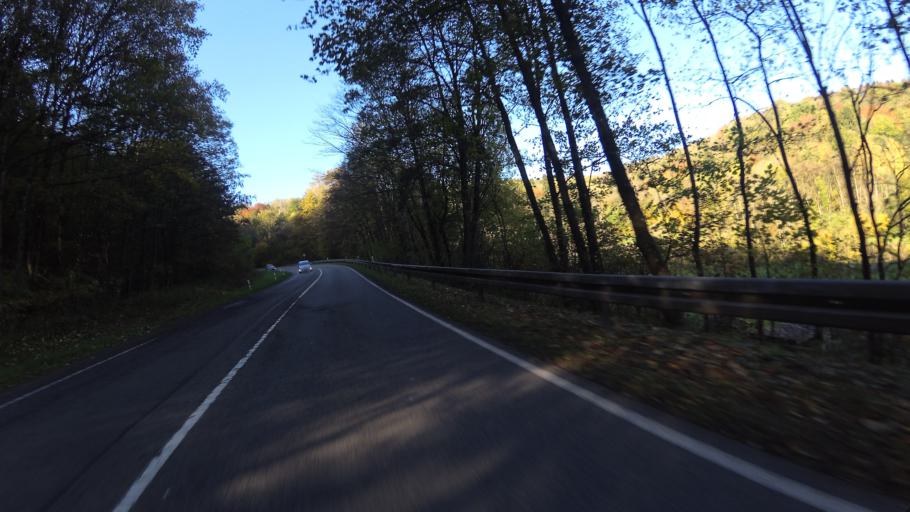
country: DE
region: Saarland
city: Losheim
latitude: 49.4703
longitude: 6.7492
